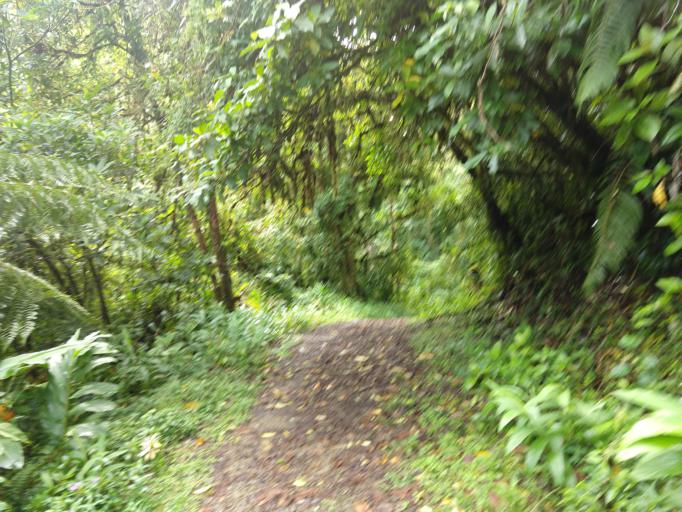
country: CR
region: Cartago
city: Orosi
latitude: 9.7444
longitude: -83.8331
